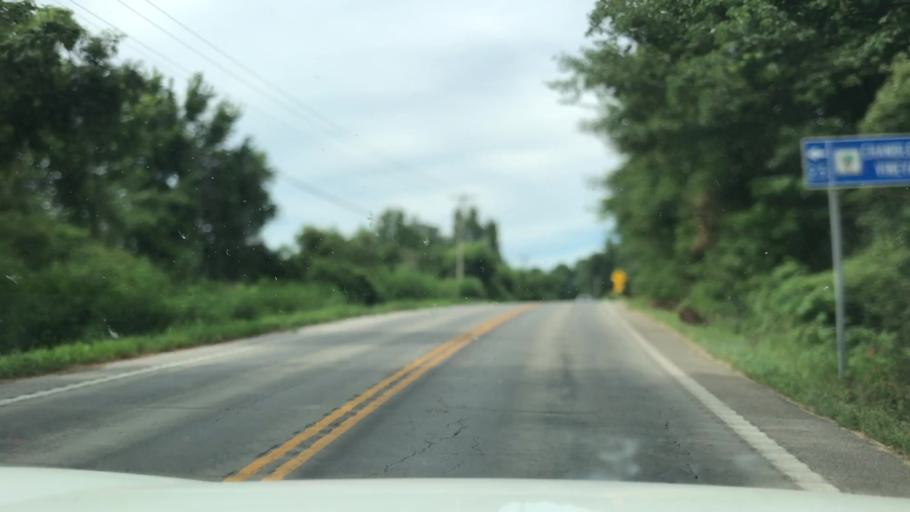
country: US
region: Missouri
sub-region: Saint Charles County
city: Weldon Spring
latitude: 38.6473
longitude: -90.7755
